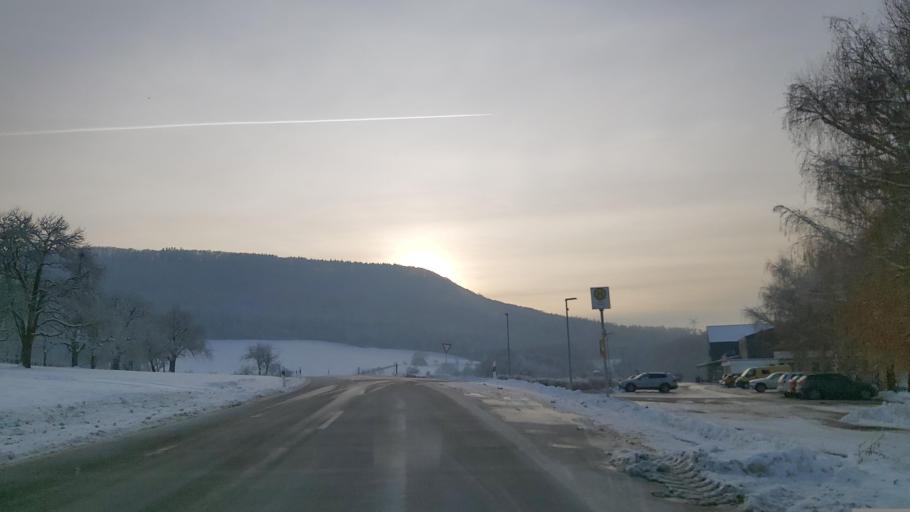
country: DE
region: Baden-Wuerttemberg
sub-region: Tuebingen Region
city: Metzingen
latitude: 48.5068
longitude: 9.2912
